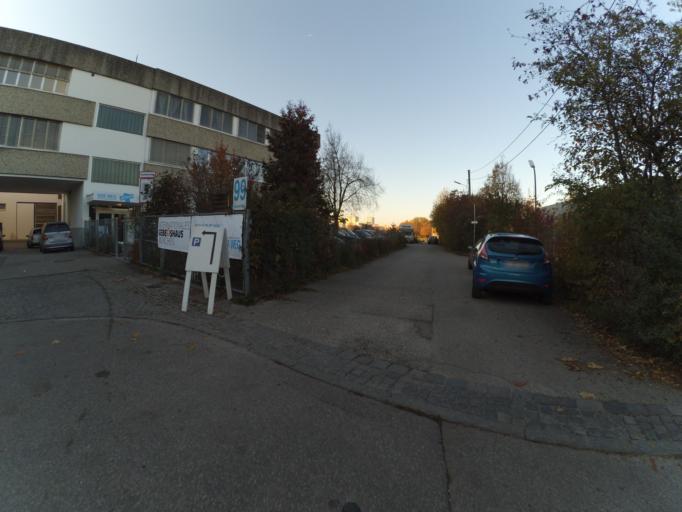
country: DE
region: Bavaria
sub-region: Upper Bavaria
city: Oberschleissheim
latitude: 48.2035
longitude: 11.5466
